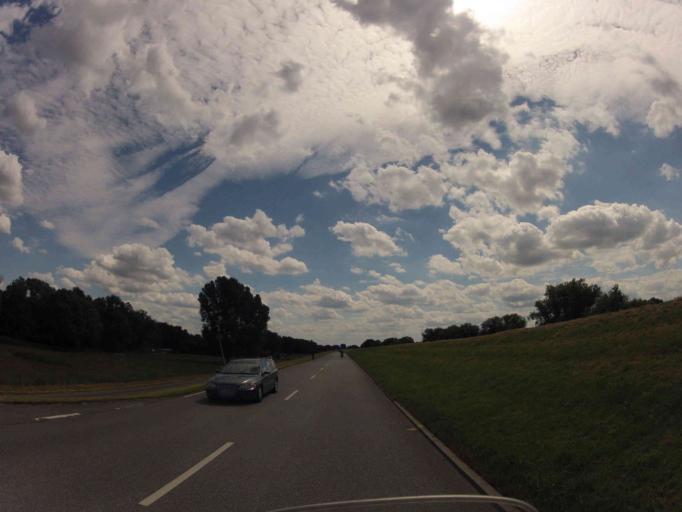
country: DE
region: Hamburg
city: Rothenburgsort
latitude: 53.4934
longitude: 10.0537
